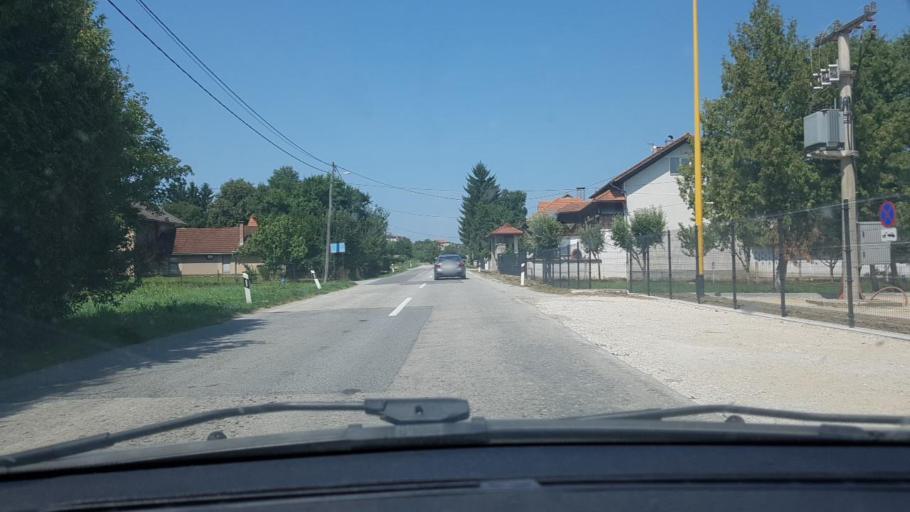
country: BA
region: Federation of Bosnia and Herzegovina
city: Velika Kladusa
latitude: 45.2011
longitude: 15.7843
